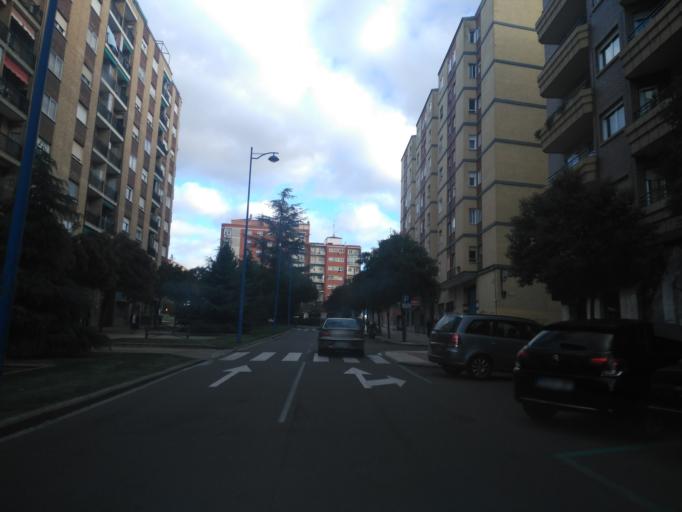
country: ES
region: Castille and Leon
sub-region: Provincia de Salamanca
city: Salamanca
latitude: 40.9759
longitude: -5.6606
